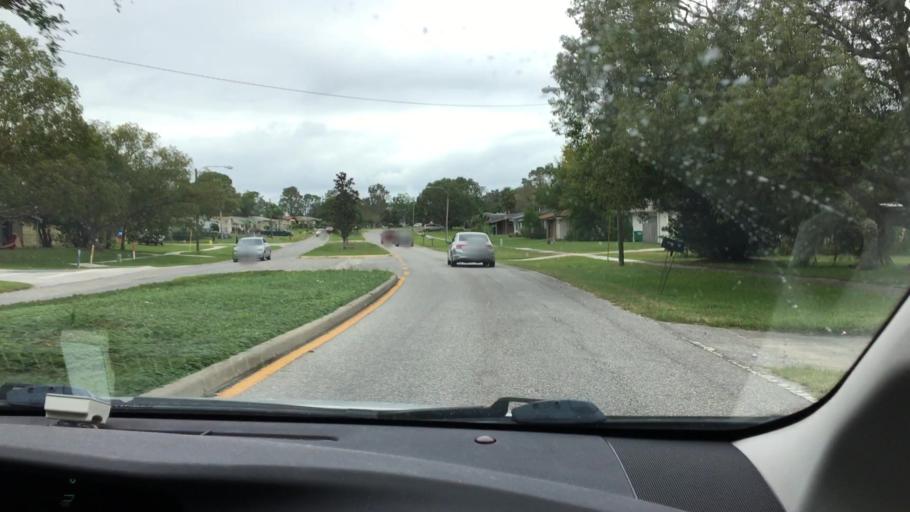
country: US
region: Florida
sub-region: Volusia County
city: Deltona
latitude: 28.8940
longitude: -81.2307
